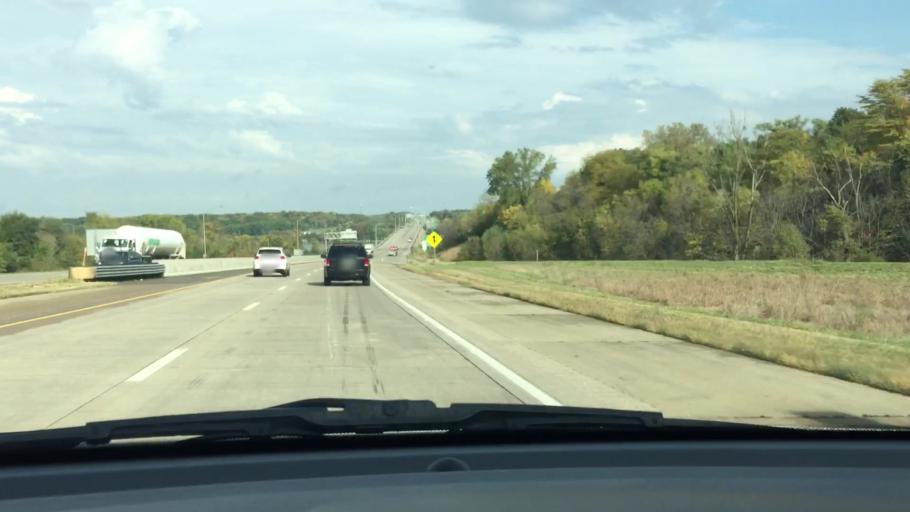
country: US
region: Iowa
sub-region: Scott County
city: Le Claire
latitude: 41.5720
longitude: -90.3596
